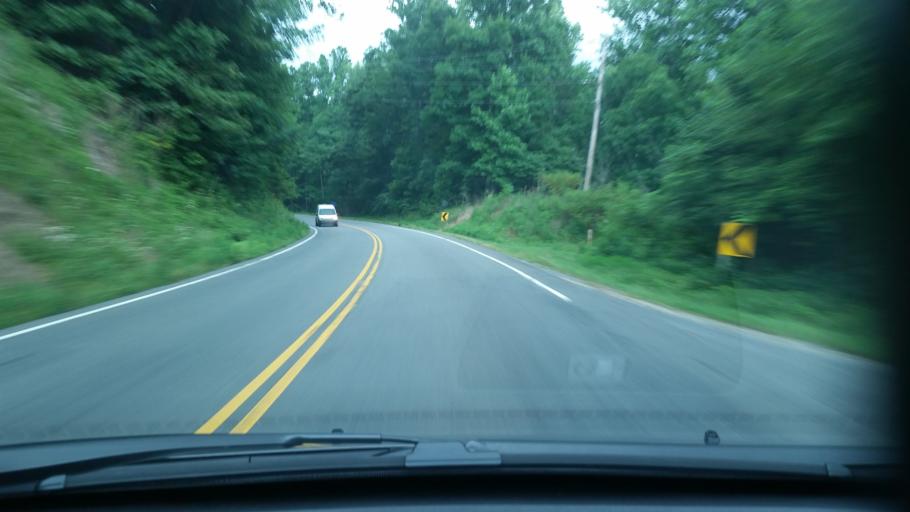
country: US
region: Virginia
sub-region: Nelson County
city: Nellysford
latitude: 37.8595
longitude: -78.8121
